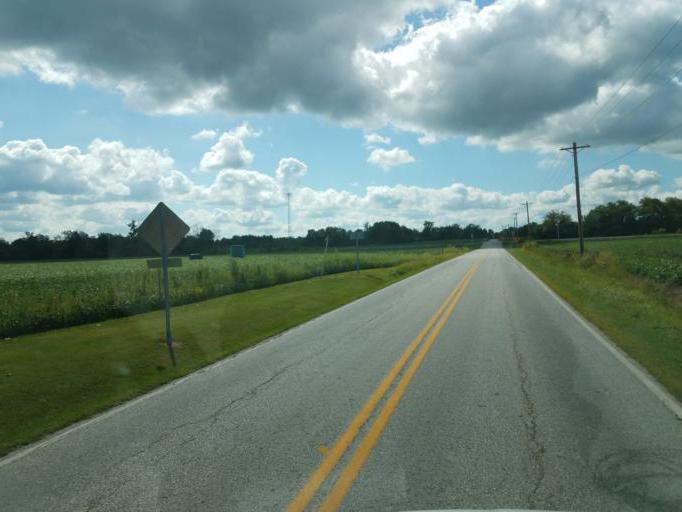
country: US
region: Ohio
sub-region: Medina County
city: Lodi
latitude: 41.1048
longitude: -82.0944
